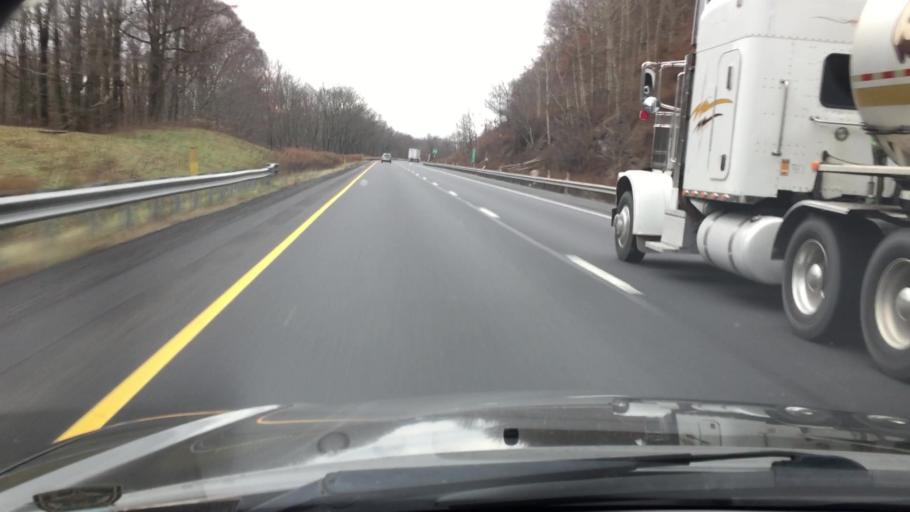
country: US
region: Pennsylvania
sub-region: Luzerne County
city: Freeland
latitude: 41.0625
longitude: -75.8746
